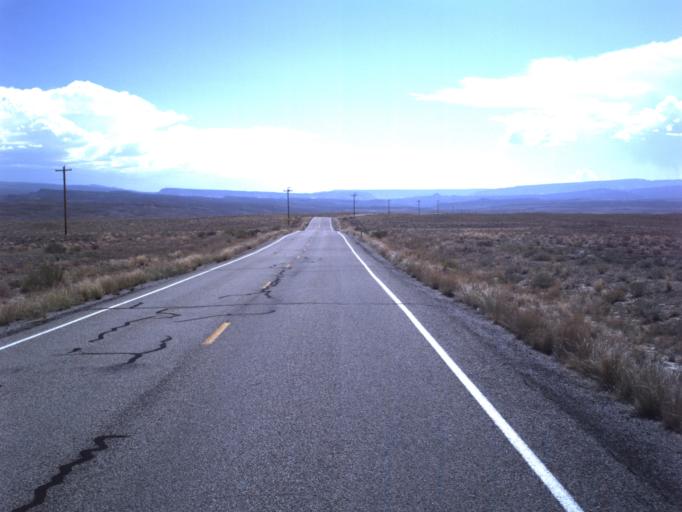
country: US
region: Utah
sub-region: Grand County
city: Moab
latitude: 38.9171
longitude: -109.3311
